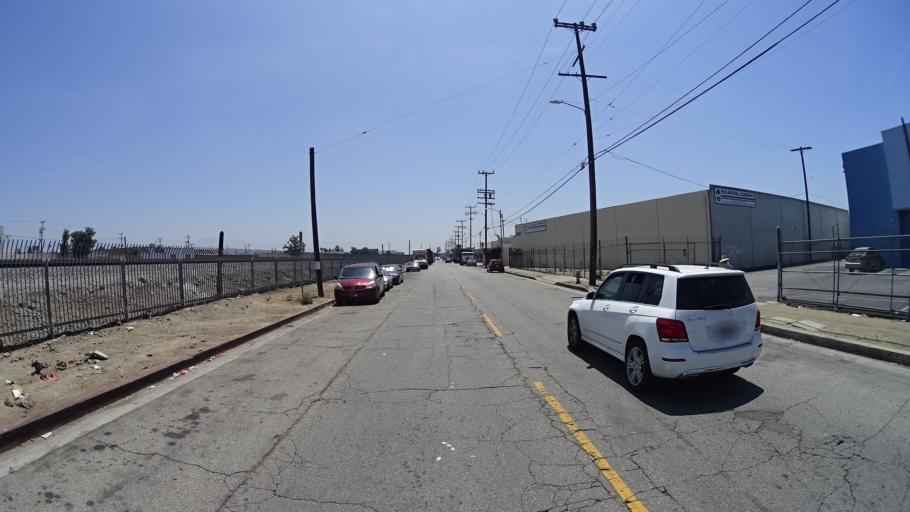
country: US
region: California
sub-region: Los Angeles County
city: Van Nuys
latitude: 34.2125
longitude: -118.4542
